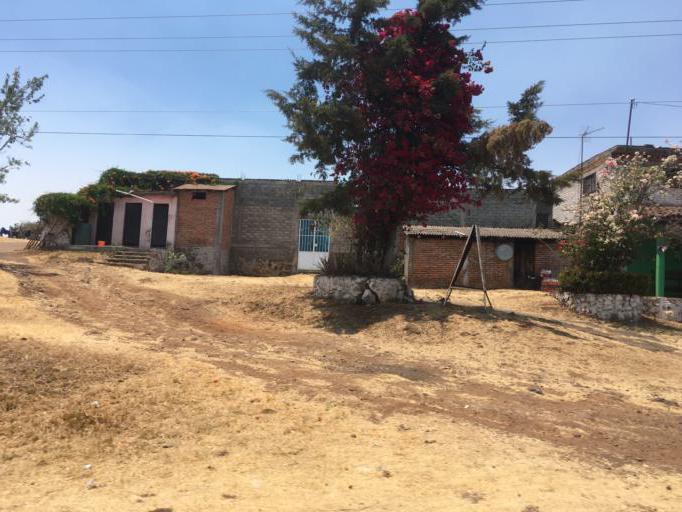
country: MX
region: Michoacan
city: Santa Fe de la Laguna
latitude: 19.6700
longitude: -101.5676
